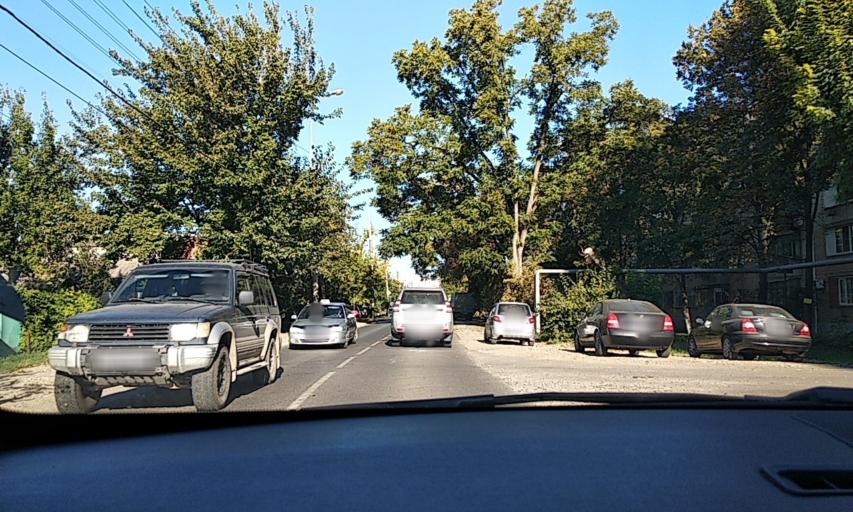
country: RU
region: Krasnodarskiy
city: Pashkovskiy
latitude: 45.0302
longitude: 39.1224
